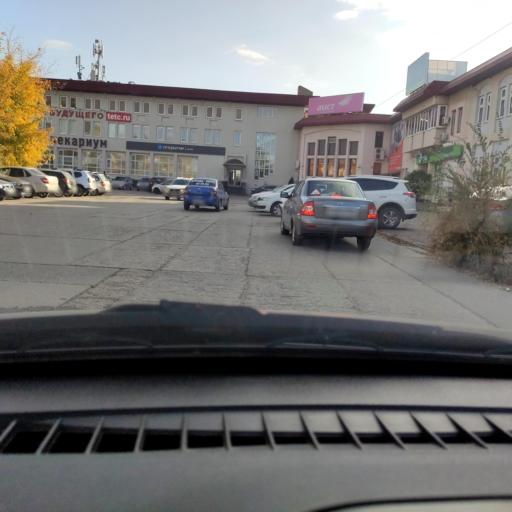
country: RU
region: Samara
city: Tol'yatti
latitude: 53.5168
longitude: 49.2797
